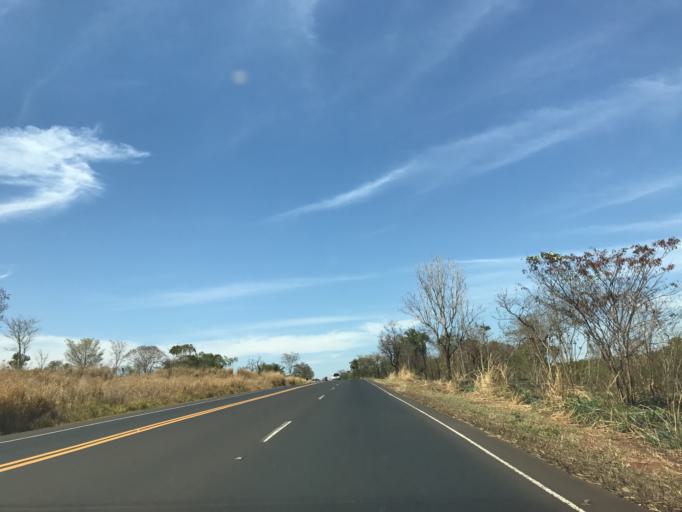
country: BR
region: Minas Gerais
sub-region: Monte Alegre De Minas
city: Monte Alegre de Minas
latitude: -19.0532
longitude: -49.0109
